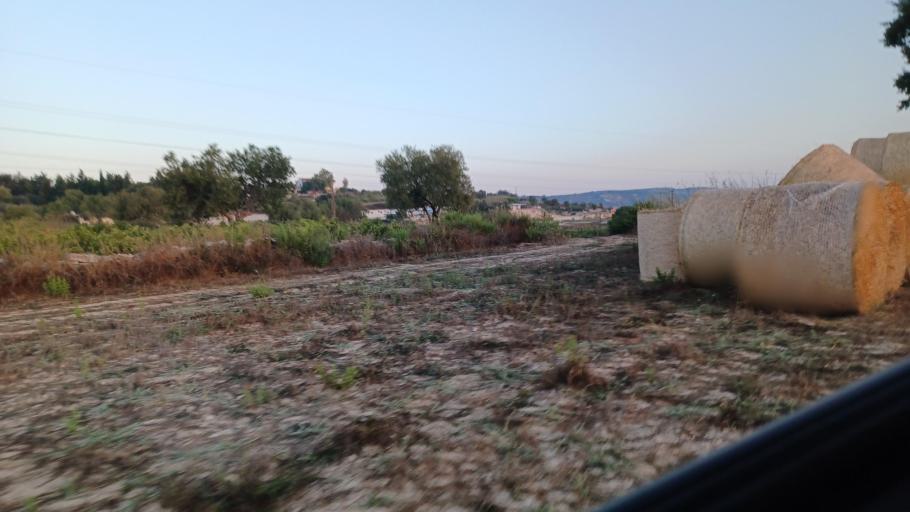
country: CY
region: Pafos
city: Mesogi
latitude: 34.8356
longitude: 32.4885
